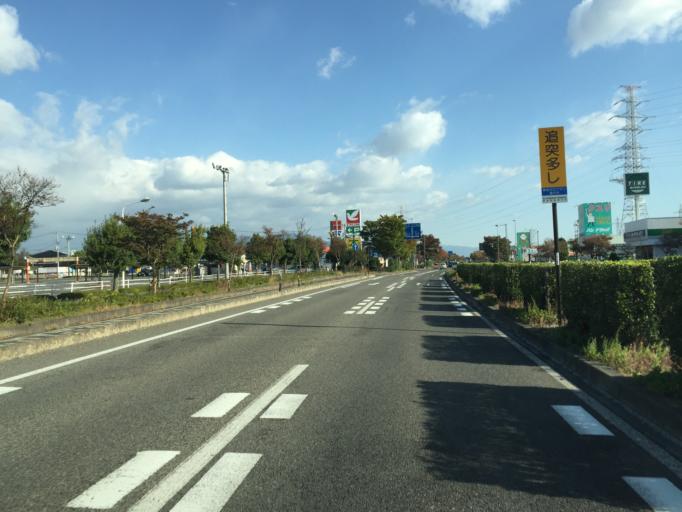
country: JP
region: Fukushima
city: Fukushima-shi
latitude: 37.7684
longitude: 140.4374
